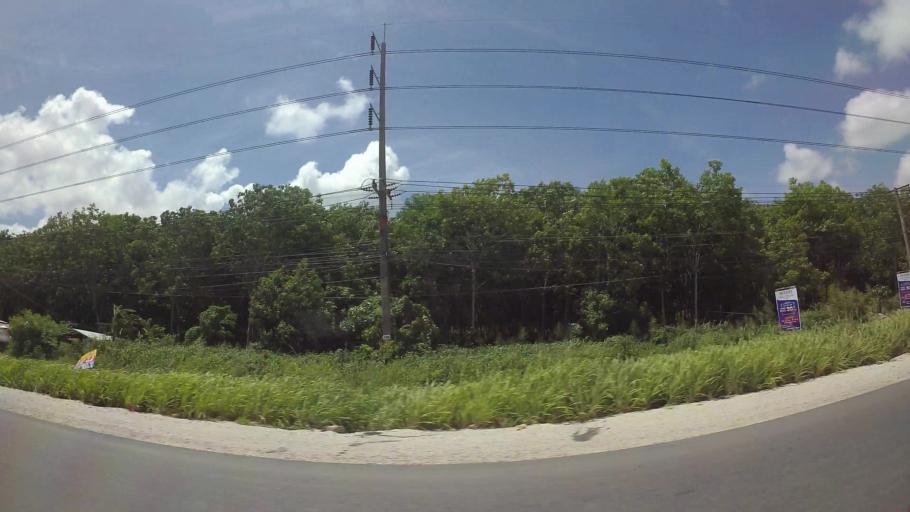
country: TH
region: Rayong
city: Rayong
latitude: 12.7235
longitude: 101.2191
